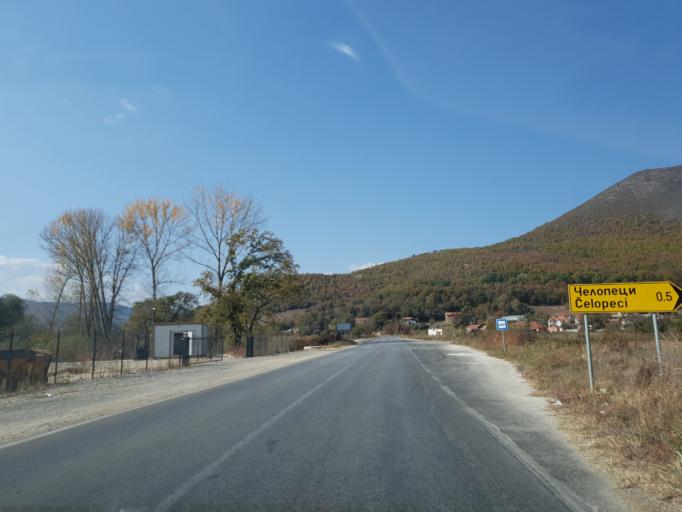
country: MK
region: Vranestica
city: Vranestica
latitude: 41.4688
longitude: 21.0308
